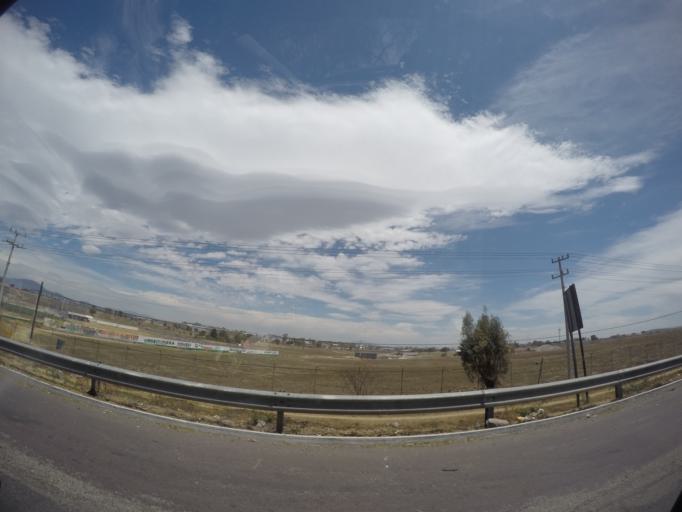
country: MX
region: Mexico
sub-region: Cuautitlan
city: Barrio Tlatenco
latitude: 19.7384
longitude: -99.2113
